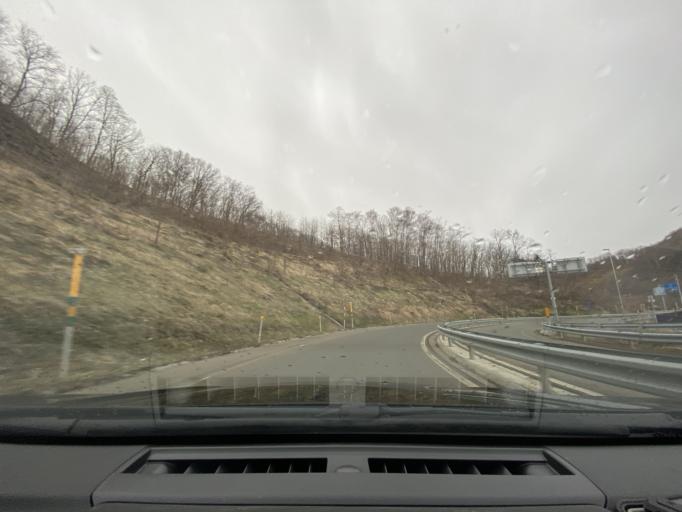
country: JP
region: Hokkaido
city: Kitami
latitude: 43.7944
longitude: 143.9161
